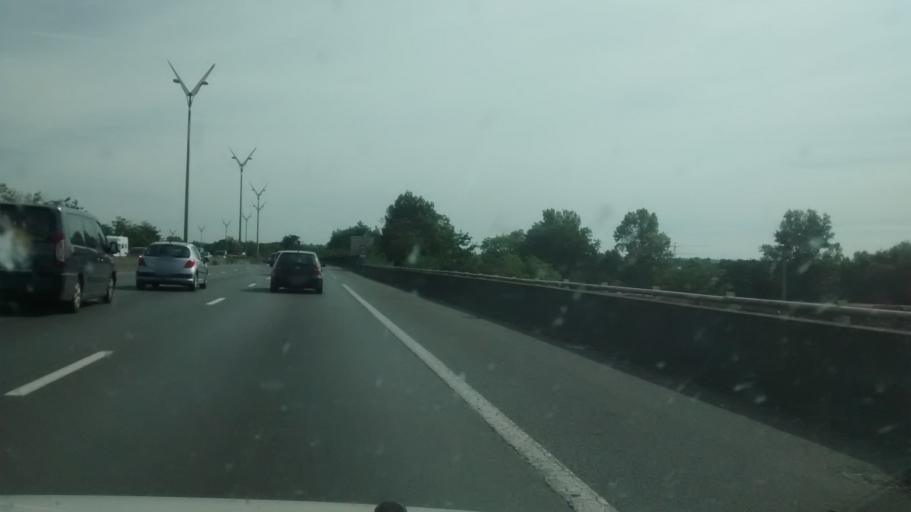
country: FR
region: Aquitaine
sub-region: Departement de la Gironde
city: Villenave-d'Ornon
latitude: 44.7795
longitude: -0.5498
